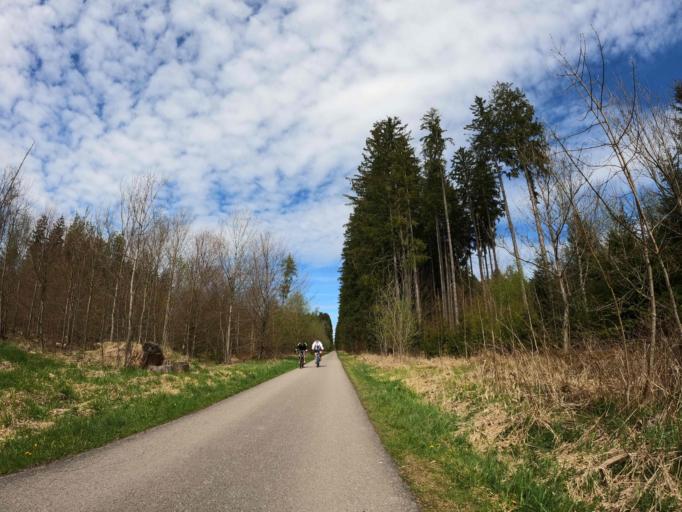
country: DE
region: Bavaria
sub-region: Upper Bavaria
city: Grunwald
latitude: 48.0194
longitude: 11.5317
